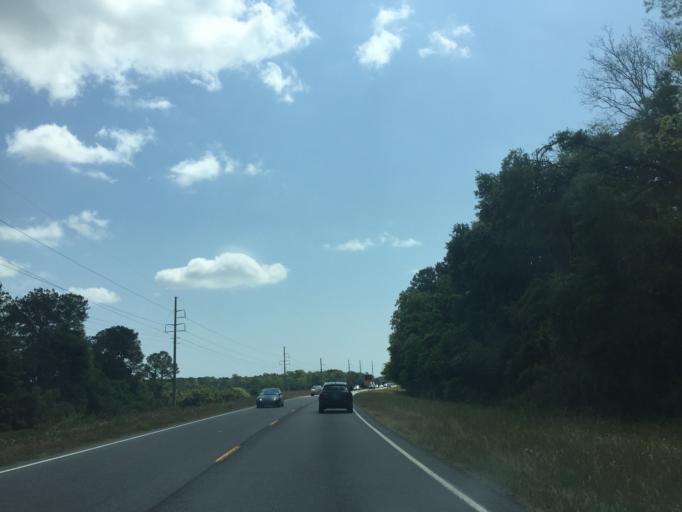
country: US
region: Georgia
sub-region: Chatham County
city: Montgomery
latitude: 31.9549
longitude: -81.0918
